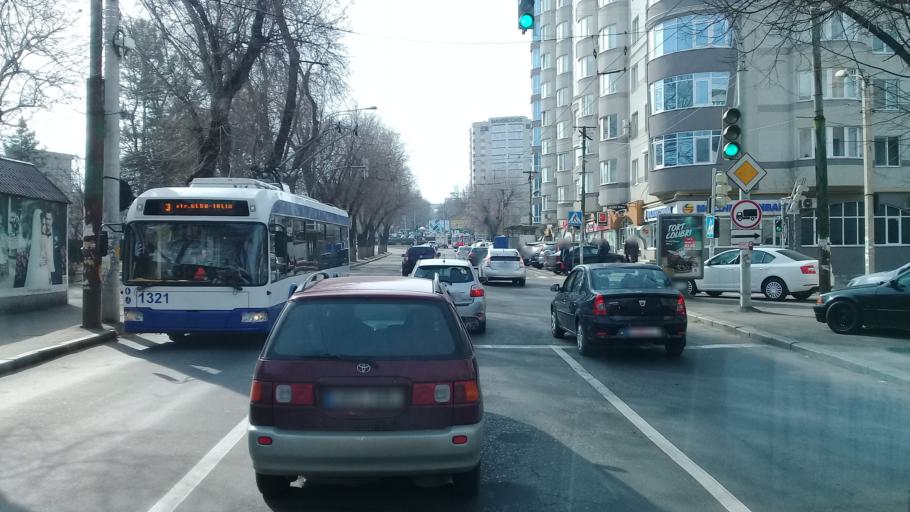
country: MD
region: Chisinau
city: Chisinau
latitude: 47.0089
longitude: 28.8277
